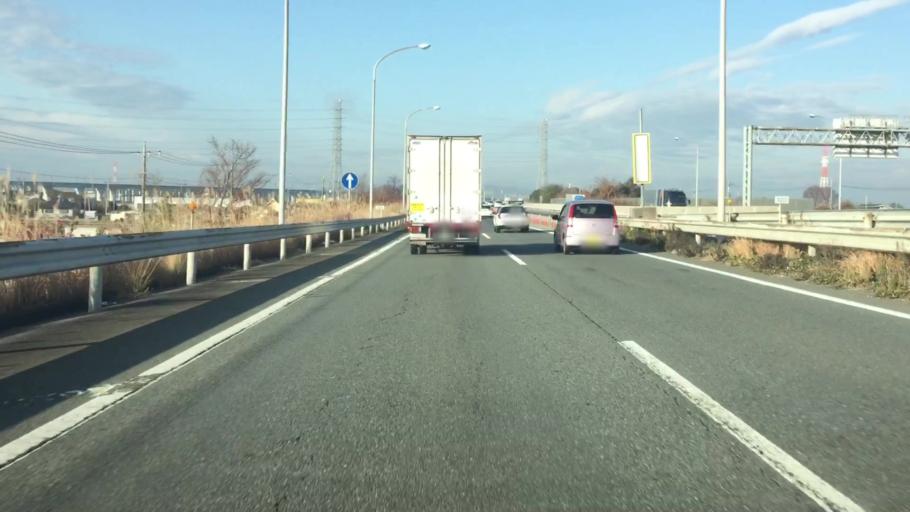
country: JP
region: Gunma
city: Fujioka
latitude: 36.2728
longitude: 139.0916
